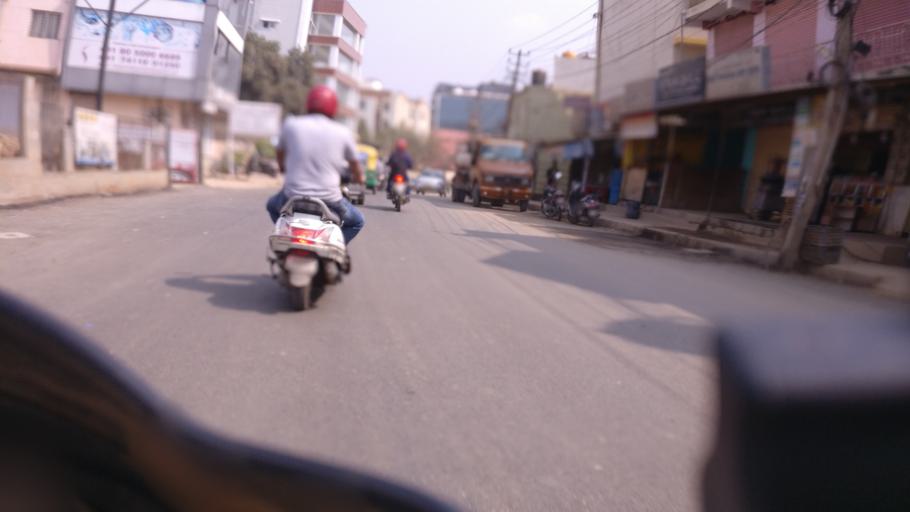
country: IN
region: Karnataka
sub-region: Bangalore Urban
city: Bangalore
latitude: 12.9121
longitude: 77.6766
